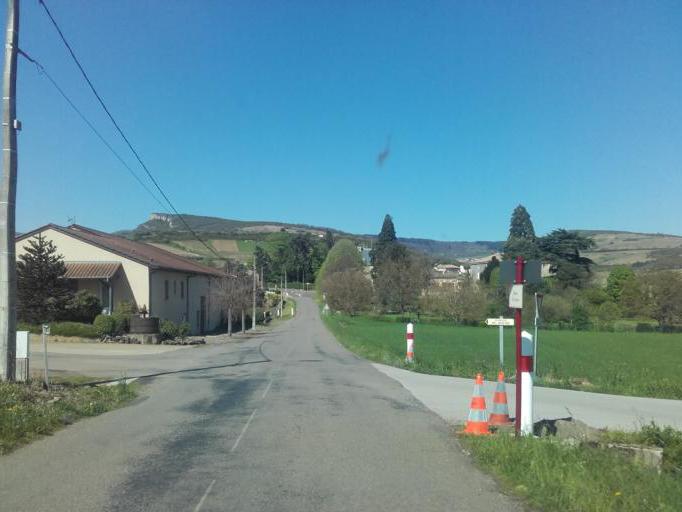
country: FR
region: Bourgogne
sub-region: Departement de Saone-et-Loire
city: Prisse
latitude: 46.2998
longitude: 4.7482
